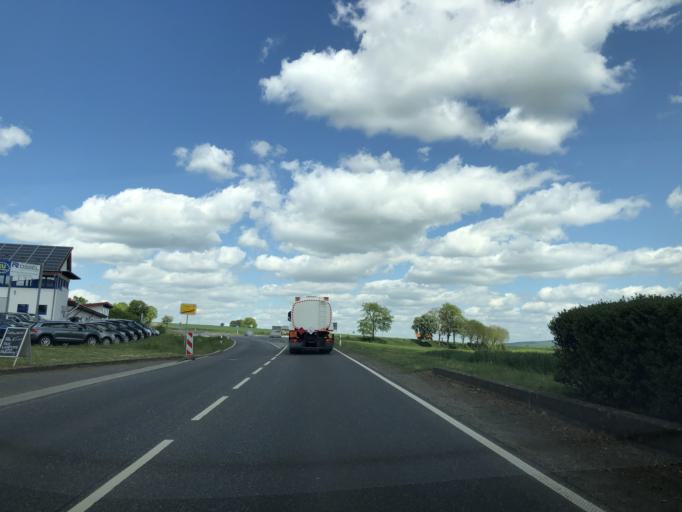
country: DE
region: Hesse
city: Gudensberg
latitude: 51.1948
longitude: 9.4120
